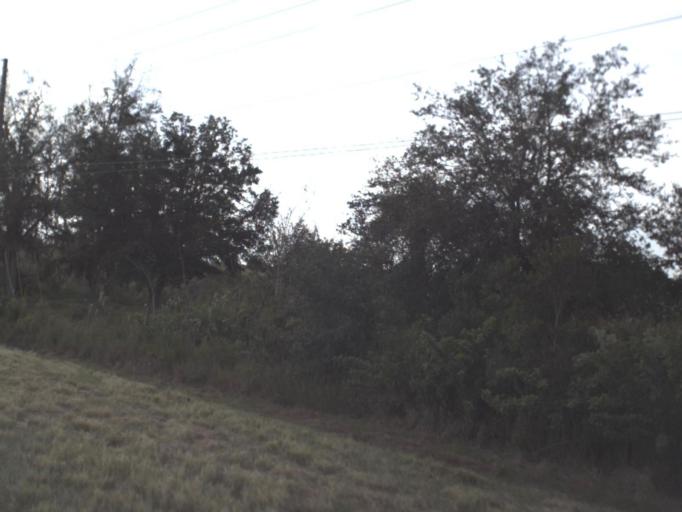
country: US
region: Florida
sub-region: Osceola County
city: Campbell
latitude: 28.2662
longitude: -81.4862
